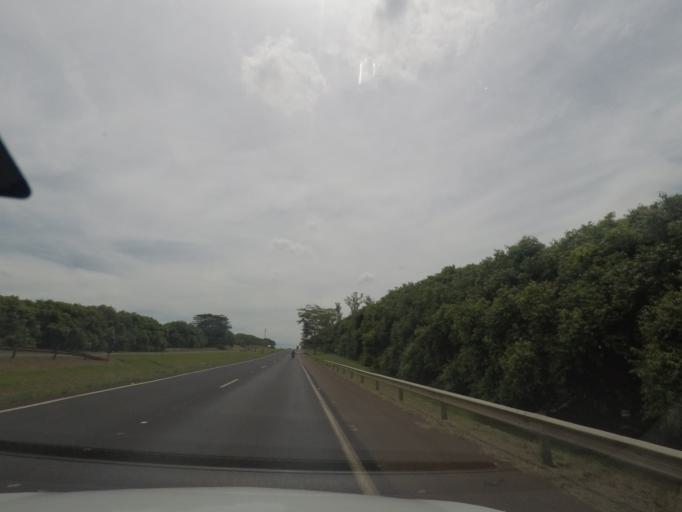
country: BR
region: Sao Paulo
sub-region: Bebedouro
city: Bebedouro
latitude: -20.9979
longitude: -48.4313
